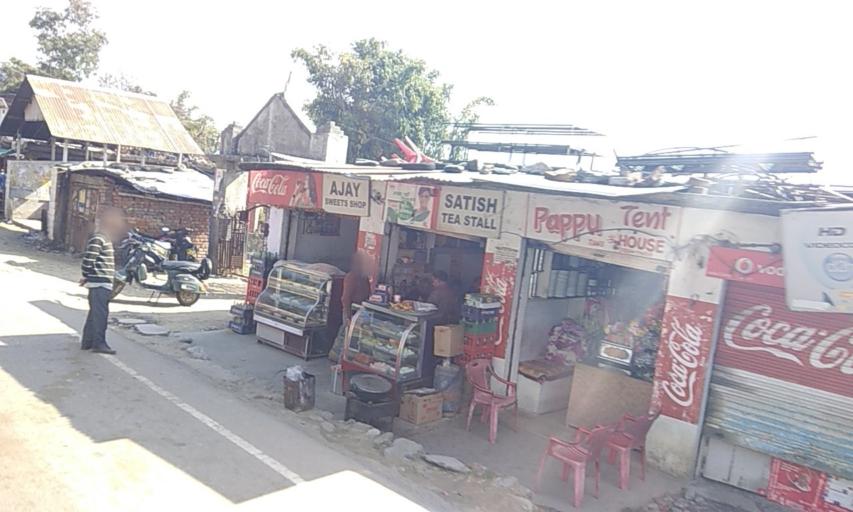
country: IN
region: Himachal Pradesh
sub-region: Kangra
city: Dharmsala
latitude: 32.1639
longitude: 76.4001
